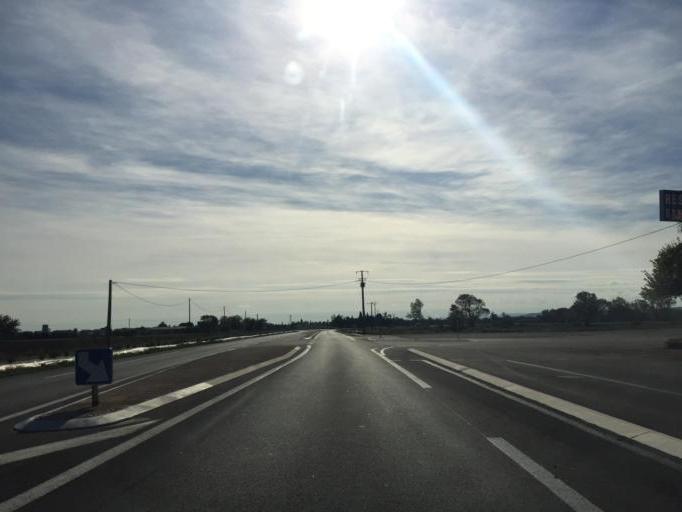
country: FR
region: Rhone-Alpes
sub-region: Departement de la Drome
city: Pierrelatte
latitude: 44.3991
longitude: 4.7040
